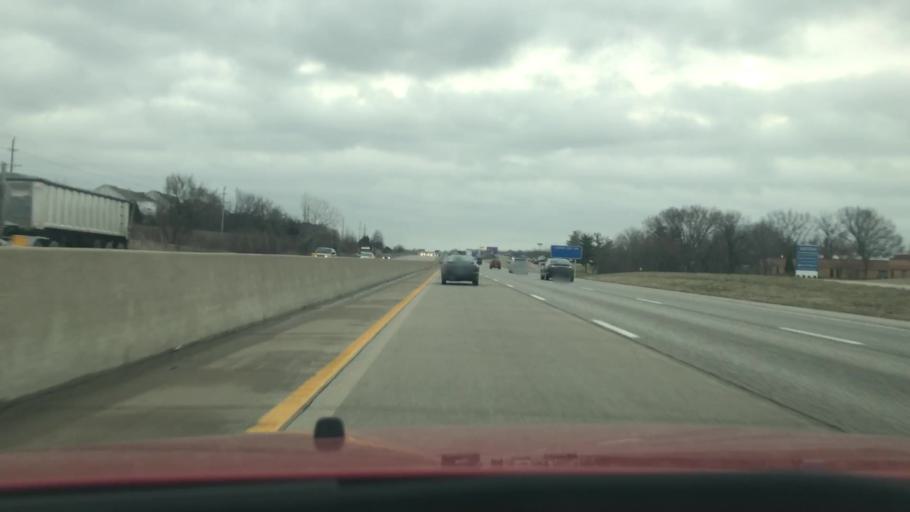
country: US
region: Missouri
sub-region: Saint Charles County
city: Lake Saint Louis
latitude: 38.8044
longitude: -90.7856
